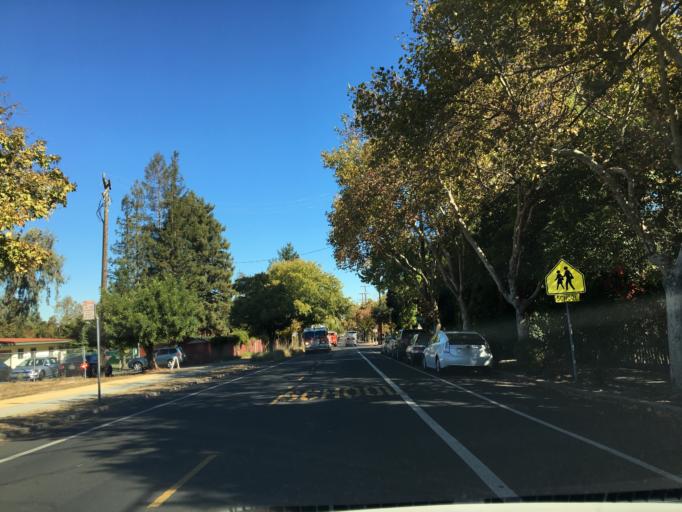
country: US
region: California
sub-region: Santa Clara County
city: Stanford
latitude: 37.4198
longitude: -122.1558
